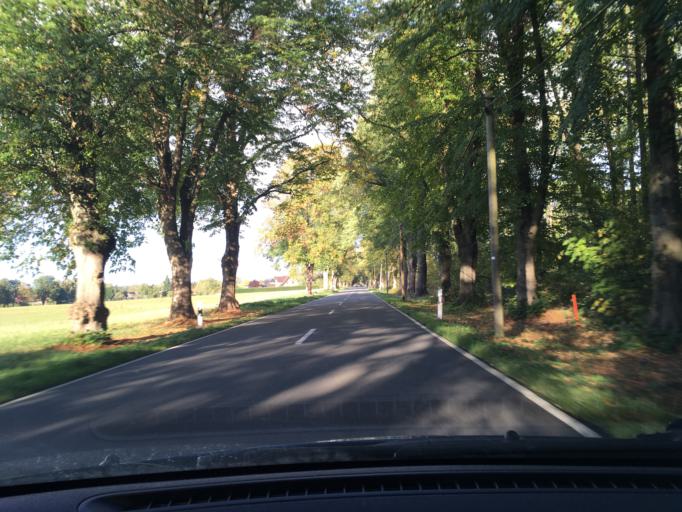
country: DE
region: Mecklenburg-Vorpommern
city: Boizenburg
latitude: 53.3981
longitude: 10.8175
